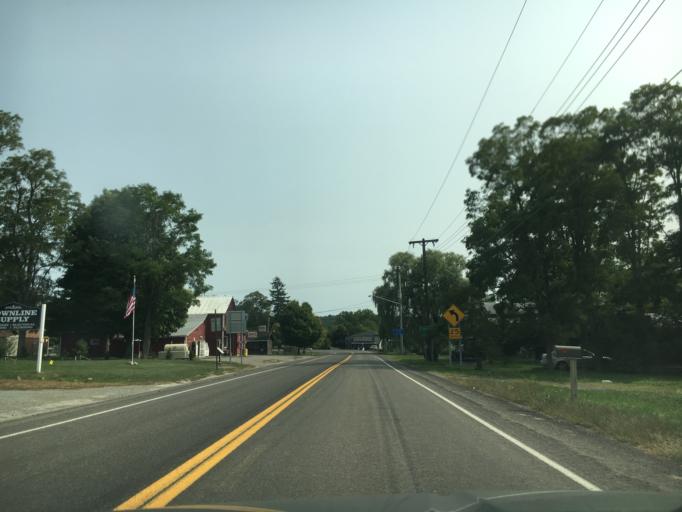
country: US
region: New York
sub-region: Steuben County
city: Sylvan Beach
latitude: 42.4717
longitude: -77.1071
